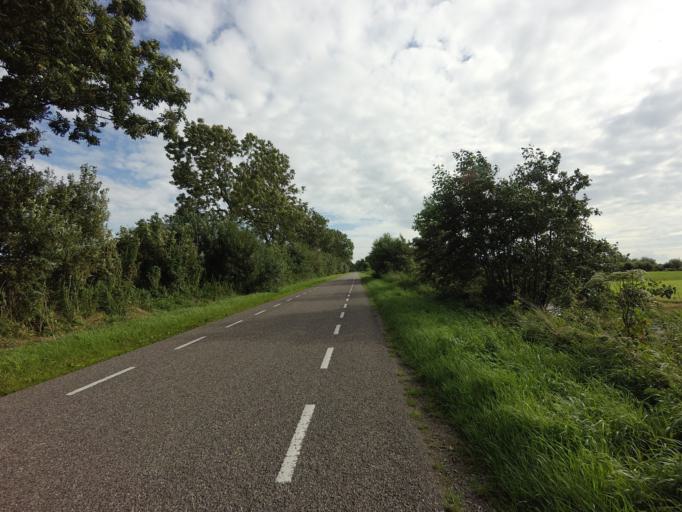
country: NL
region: Utrecht
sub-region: Stichtse Vecht
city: Breukelen
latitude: 52.1937
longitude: 4.9594
